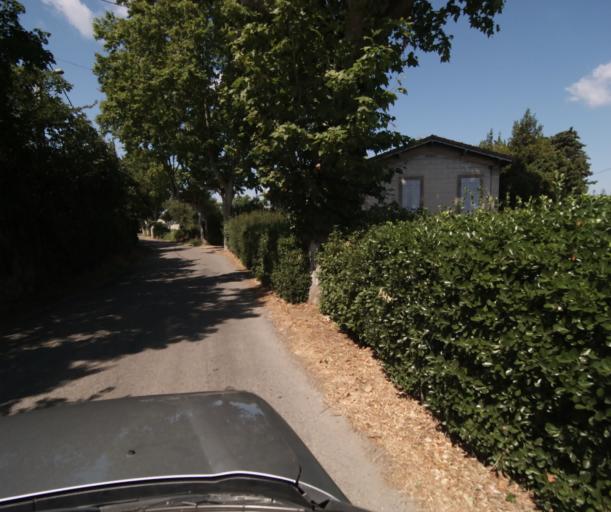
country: FR
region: Languedoc-Roussillon
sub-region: Departement de l'Aude
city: Limoux
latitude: 43.0539
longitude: 2.2091
